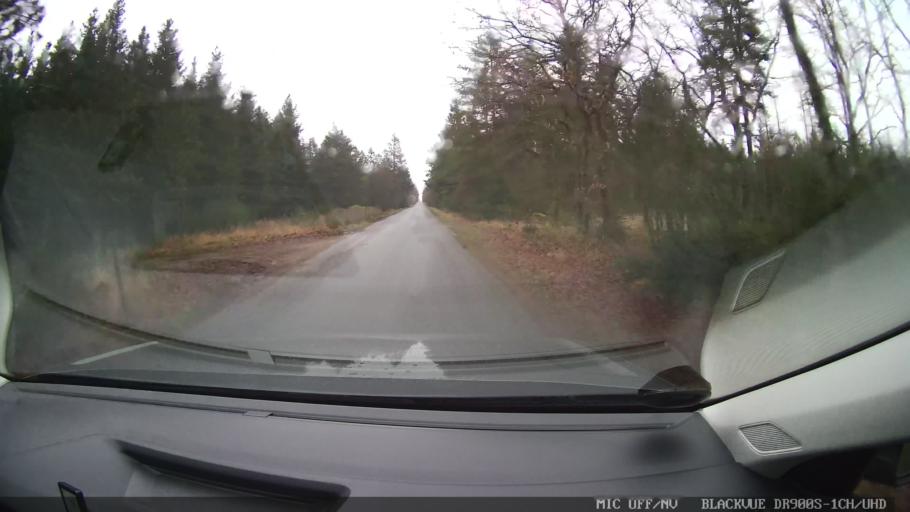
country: DK
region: Central Jutland
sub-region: Viborg Kommune
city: Karup
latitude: 56.2374
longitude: 9.1286
